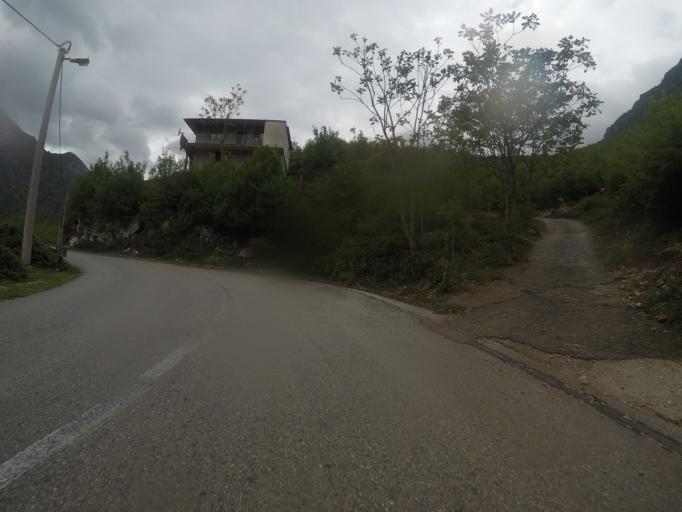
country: BA
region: Federation of Bosnia and Herzegovina
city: Jablanica
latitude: 43.5322
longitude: 17.6678
